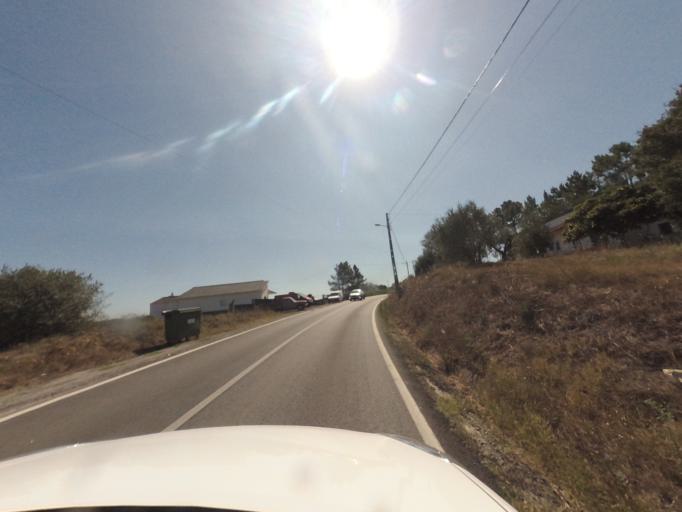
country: PT
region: Leiria
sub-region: Alcobaca
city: Turquel
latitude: 39.4906
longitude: -8.9783
